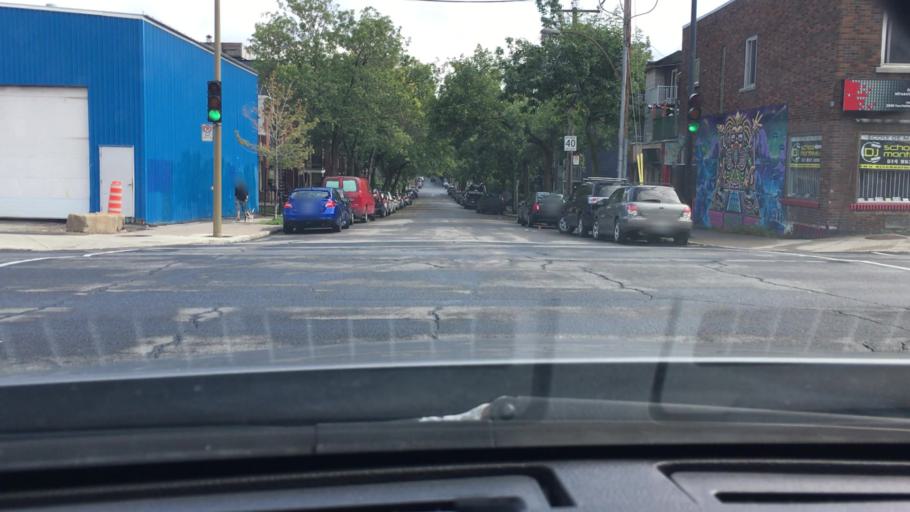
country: CA
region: Quebec
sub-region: Monteregie
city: Longueuil
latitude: 45.5387
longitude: -73.5565
